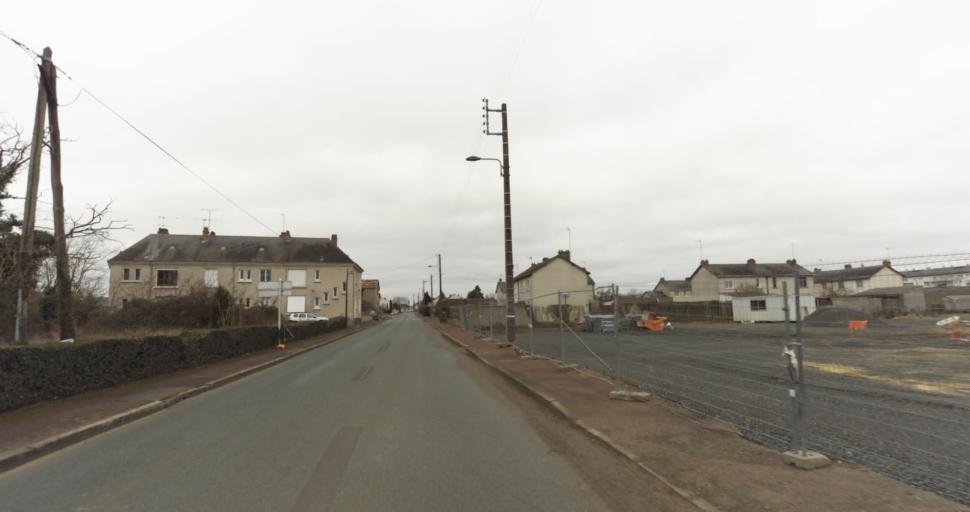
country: FR
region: Pays de la Loire
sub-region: Departement de Maine-et-Loire
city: Montreuil-Bellay
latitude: 47.1251
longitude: -0.1455
